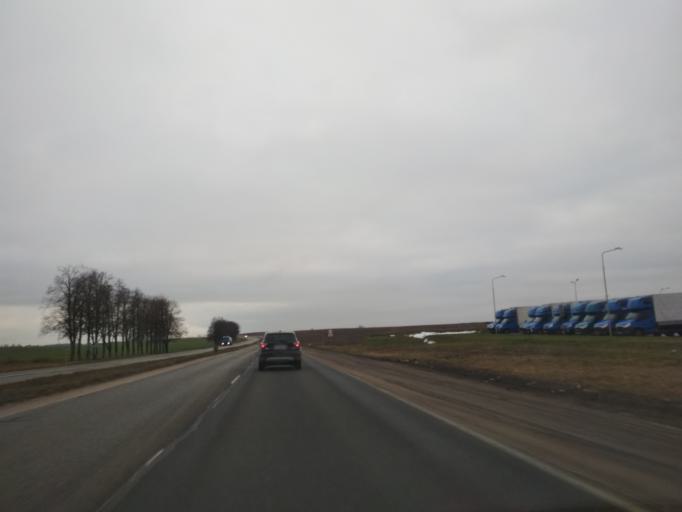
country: BY
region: Minsk
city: Luhavaya Slabada
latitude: 53.7568
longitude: 27.8306
